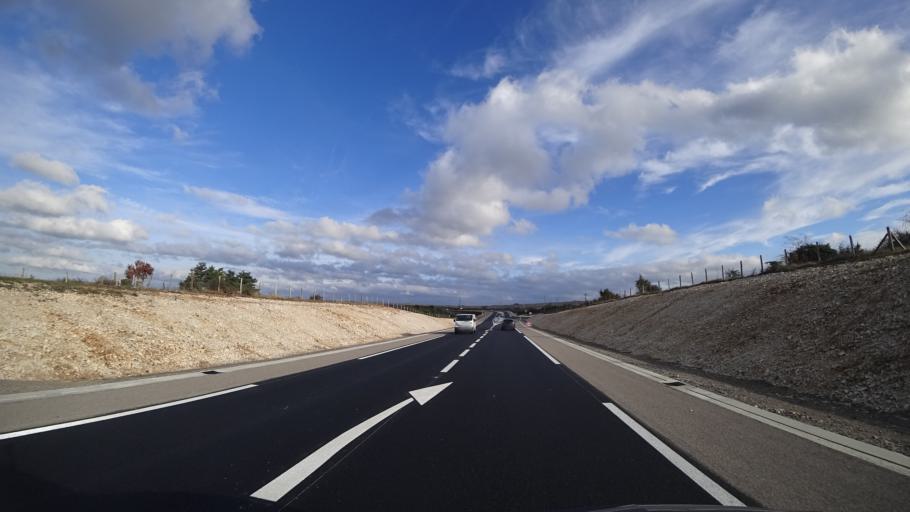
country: FR
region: Midi-Pyrenees
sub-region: Departement de l'Aveyron
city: Sebazac-Concoures
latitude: 44.4161
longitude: 2.6487
